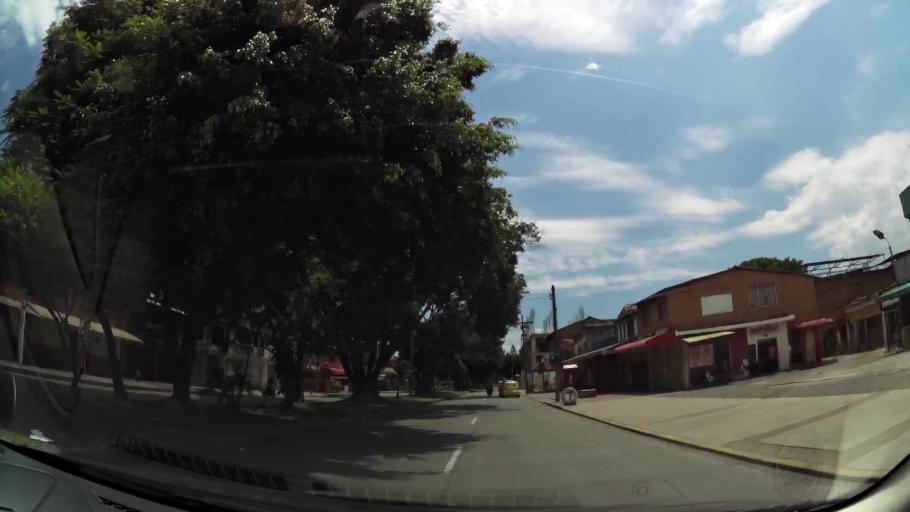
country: CO
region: Valle del Cauca
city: Cali
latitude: 3.4522
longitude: -76.5050
